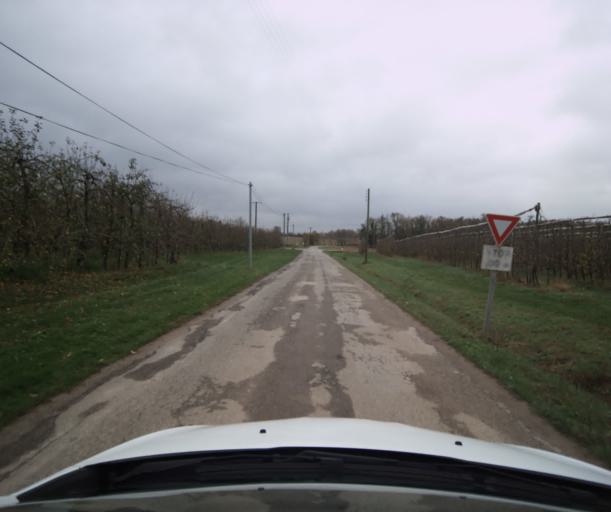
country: FR
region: Midi-Pyrenees
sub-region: Departement du Tarn-et-Garonne
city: Moissac
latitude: 44.0828
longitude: 1.1556
